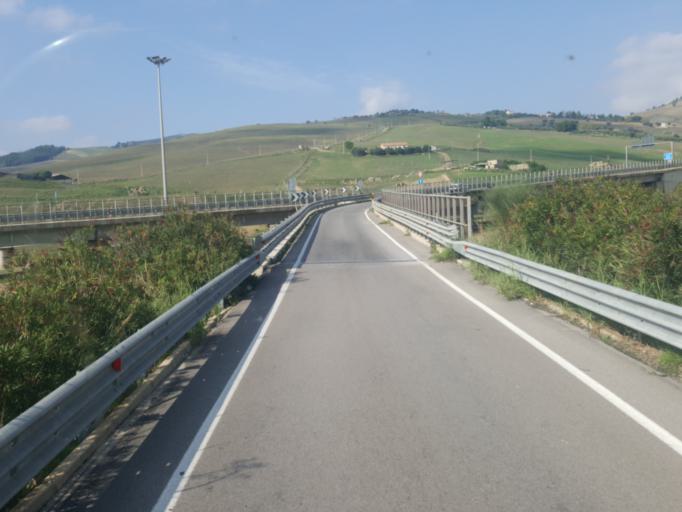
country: IT
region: Sicily
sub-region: Enna
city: Pietraperzia
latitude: 37.4578
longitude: 14.1088
